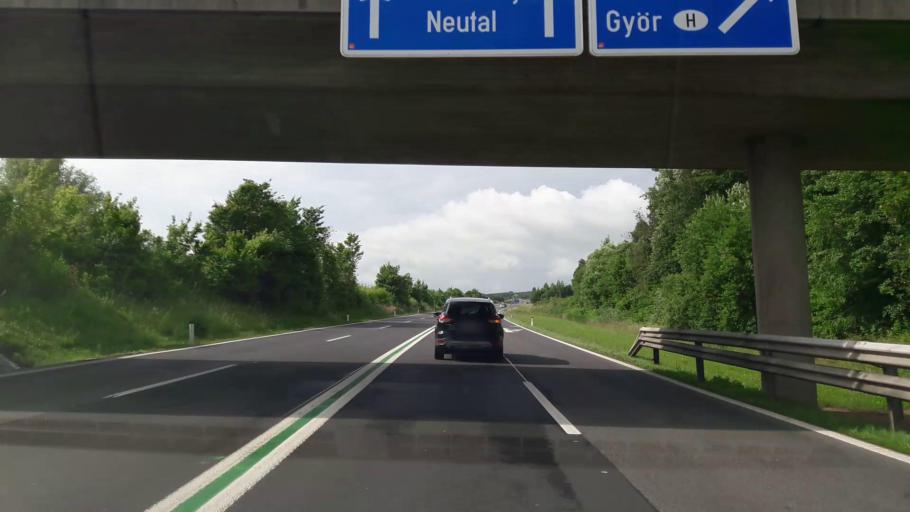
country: AT
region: Burgenland
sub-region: Politischer Bezirk Oberpullendorf
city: Weppersdorf
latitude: 47.5785
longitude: 16.4168
